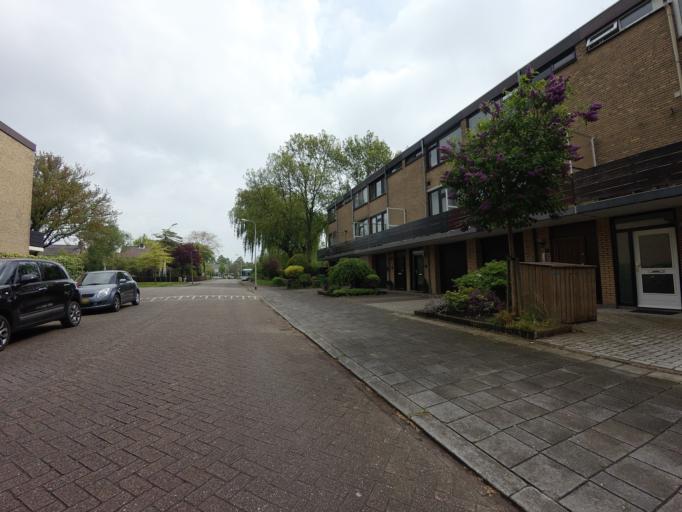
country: NL
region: South Holland
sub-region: Gemeente Ridderkerk
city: Ridderkerk
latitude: 51.8703
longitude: 4.5886
